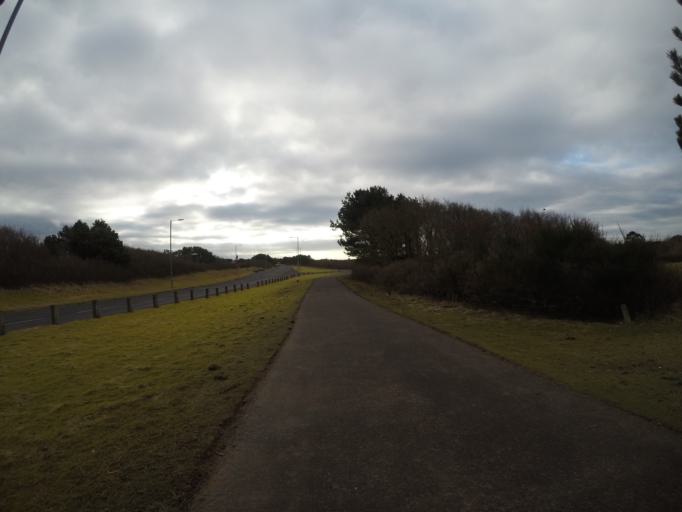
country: GB
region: Scotland
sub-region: North Ayrshire
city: Irvine
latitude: 55.6007
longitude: -4.6797
